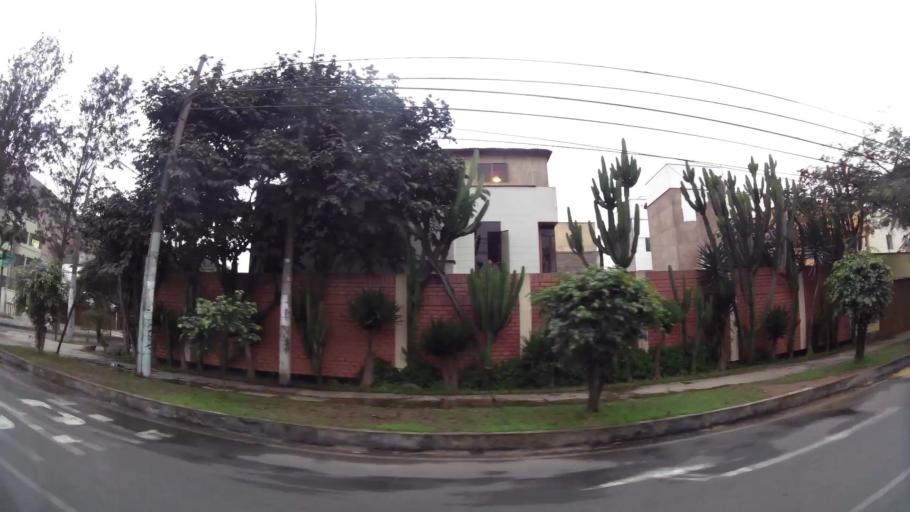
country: PE
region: Lima
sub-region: Lima
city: La Molina
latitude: -12.0949
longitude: -76.9521
